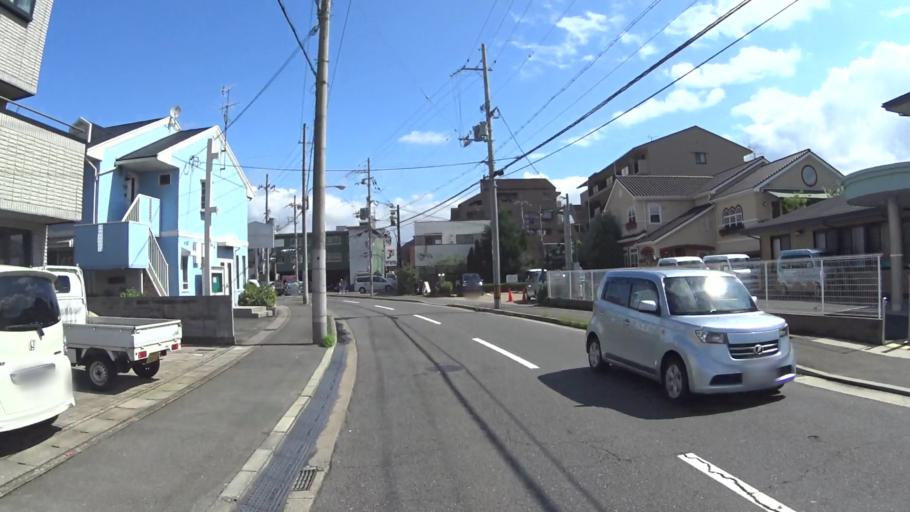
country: JP
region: Kyoto
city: Muko
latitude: 34.9949
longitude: 135.7027
